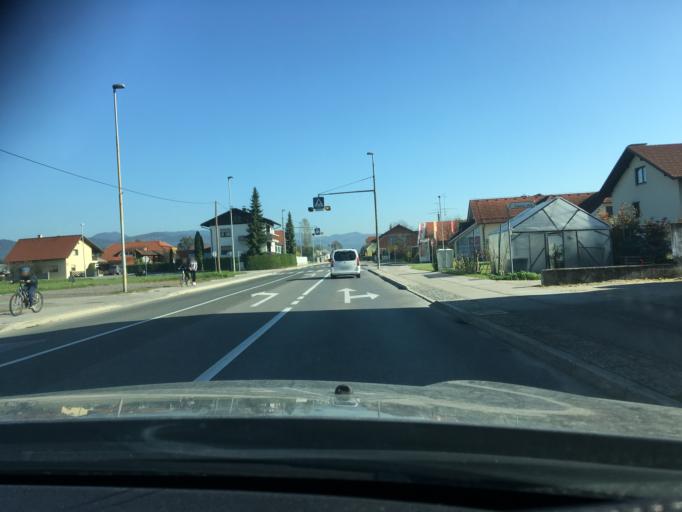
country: SI
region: Domzale
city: Dob
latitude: 46.1537
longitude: 14.6272
